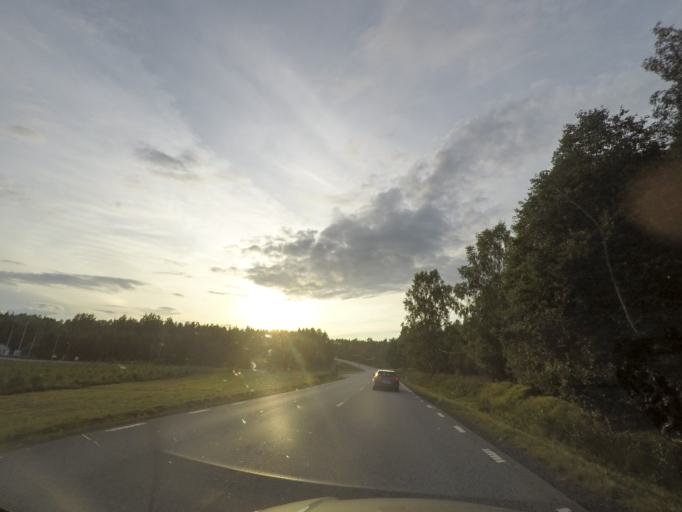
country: SE
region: OErebro
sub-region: Nora Kommun
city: As
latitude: 59.5171
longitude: 14.9515
